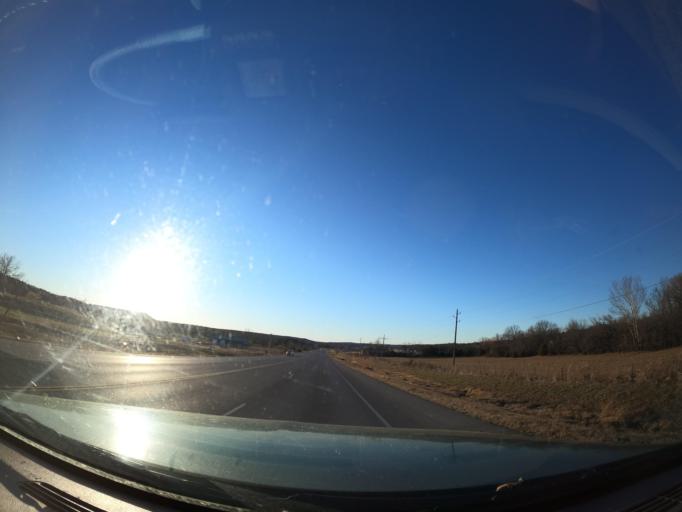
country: US
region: Oklahoma
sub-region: Pittsburg County
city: Krebs
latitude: 34.8949
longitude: -95.6549
